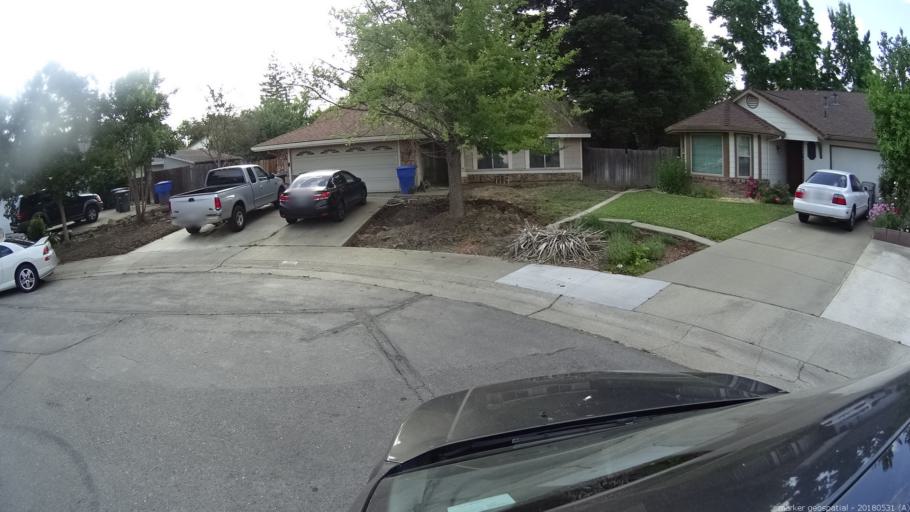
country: US
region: California
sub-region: Sacramento County
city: Sacramento
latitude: 38.6205
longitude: -121.4859
